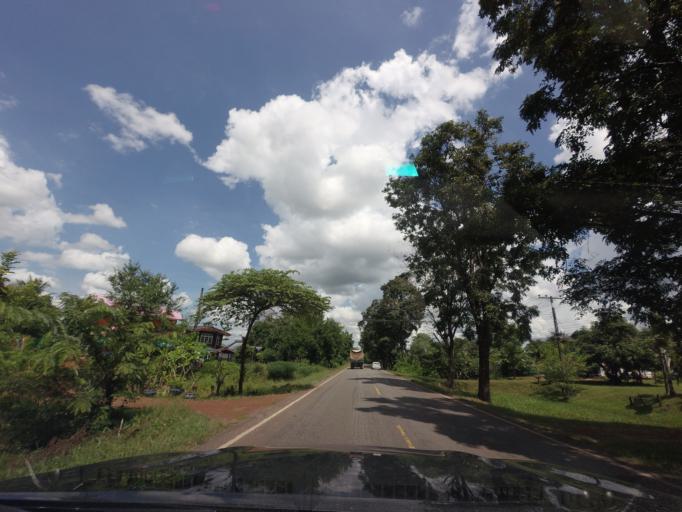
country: TH
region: Changwat Udon Thani
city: Phibun Rak
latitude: 17.5898
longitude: 103.0496
